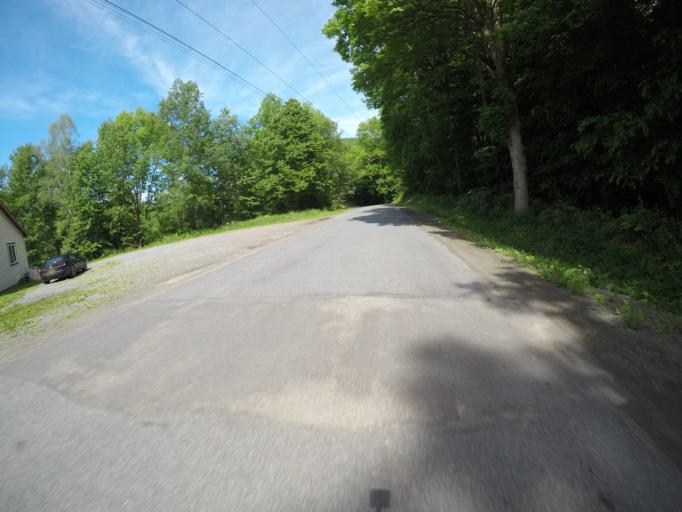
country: US
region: New York
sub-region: Delaware County
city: Stamford
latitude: 42.1323
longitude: -74.6598
